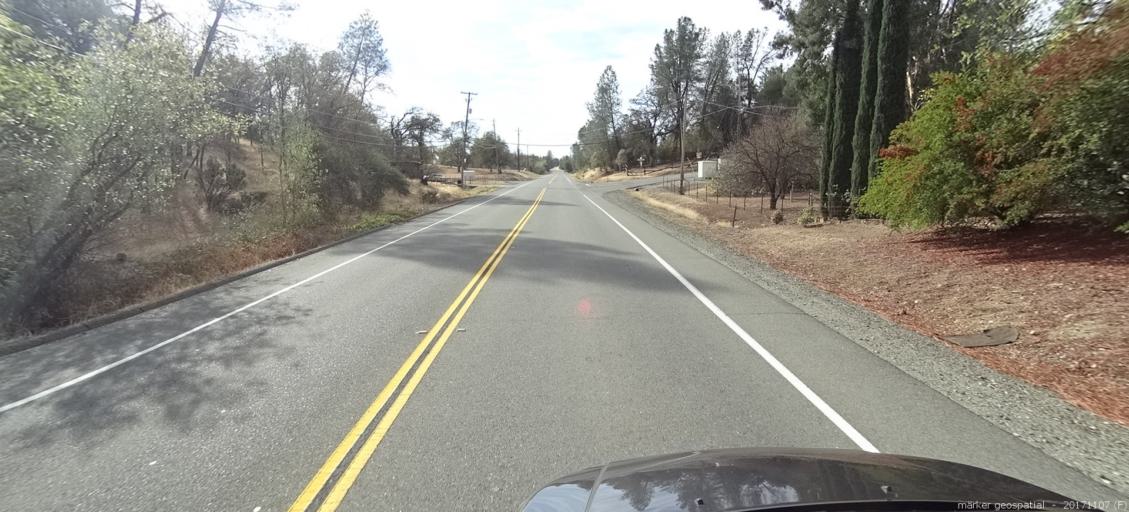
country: US
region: California
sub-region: Shasta County
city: Shasta
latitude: 40.5319
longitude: -122.4751
